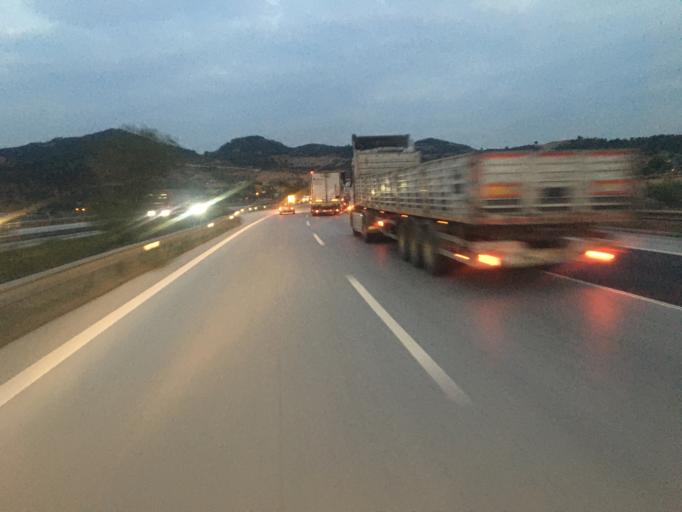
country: TR
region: Osmaniye
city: Haruniye
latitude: 37.1942
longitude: 36.4280
